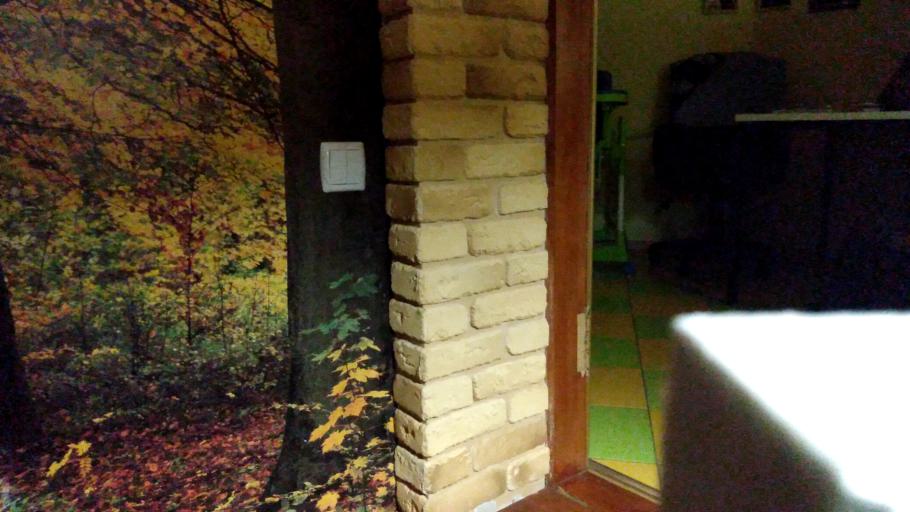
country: RU
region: Vologda
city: Lipin Bor
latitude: 60.8759
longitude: 38.0057
